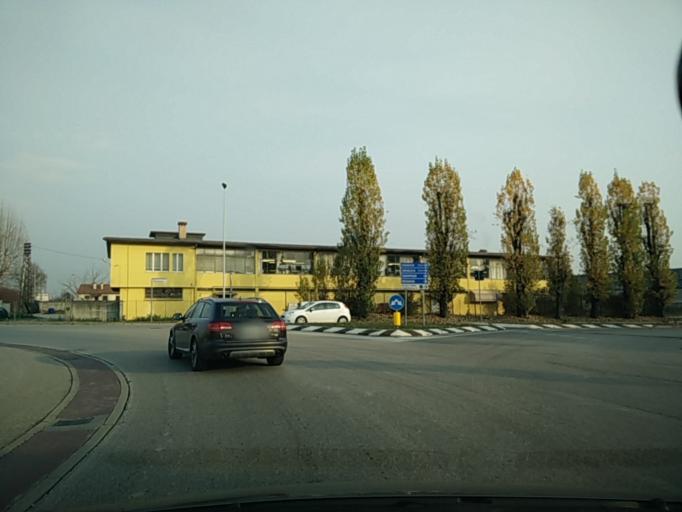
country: IT
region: Veneto
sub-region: Provincia di Treviso
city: Salvatronda
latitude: 45.6740
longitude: 11.9601
